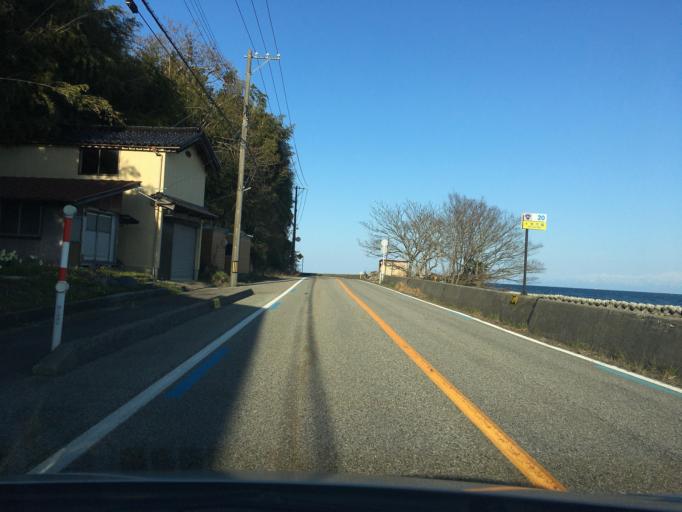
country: JP
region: Toyama
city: Himi
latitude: 36.9549
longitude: 137.0452
